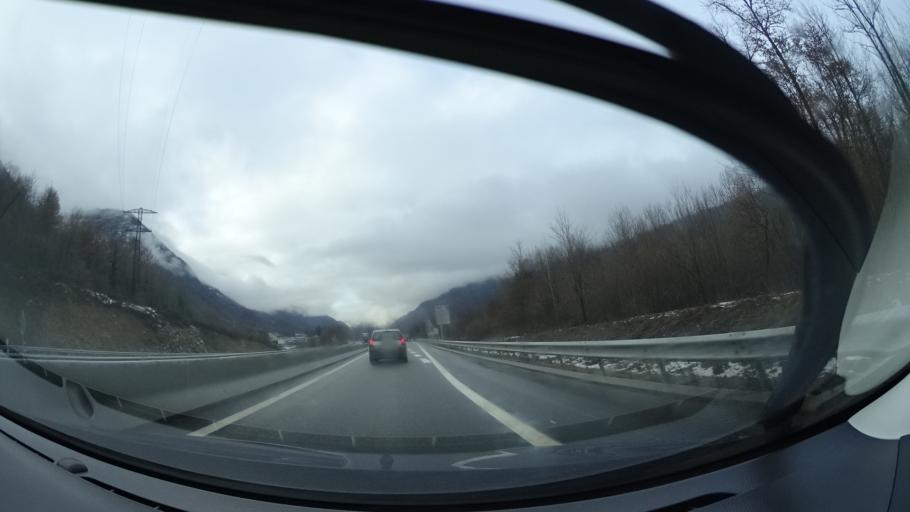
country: FR
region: Midi-Pyrenees
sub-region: Departement de l'Ariege
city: Ax-les-Thermes
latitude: 42.7281
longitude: 1.8073
